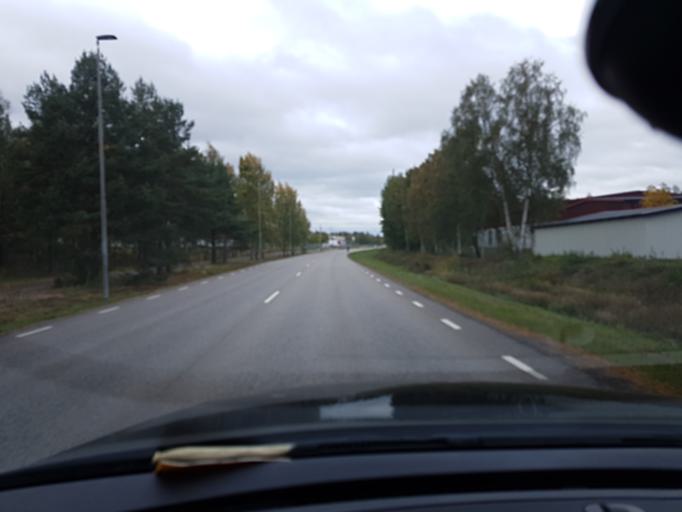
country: SE
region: Kronoberg
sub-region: Vaxjo Kommun
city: Vaexjoe
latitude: 56.9071
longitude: 14.8214
